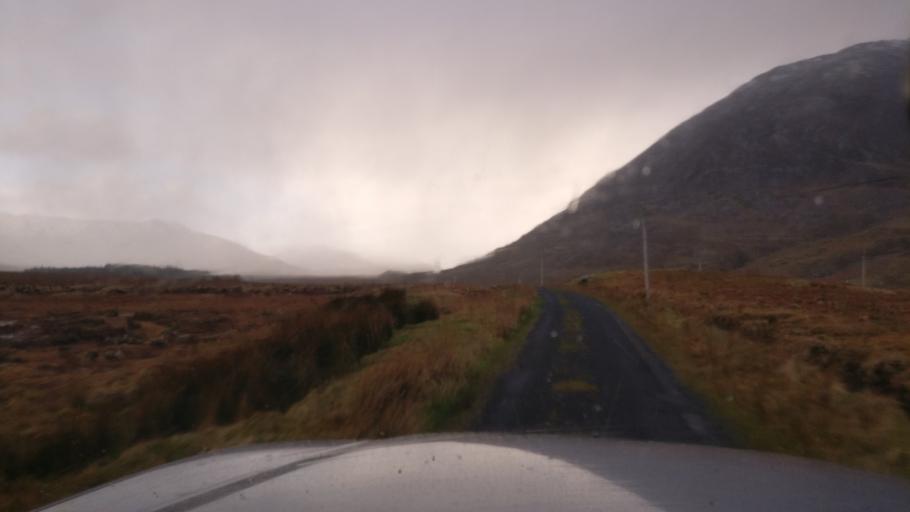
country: IE
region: Connaught
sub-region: County Galway
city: Clifden
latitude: 53.5158
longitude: -9.7170
